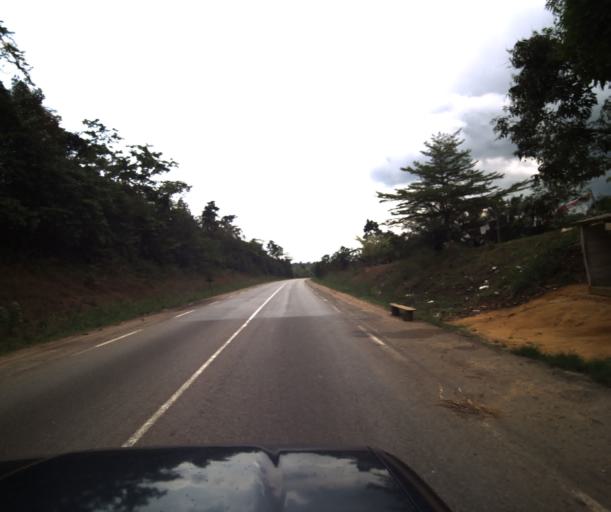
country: CM
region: Littoral
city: Edea
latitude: 3.9497
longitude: 10.0233
